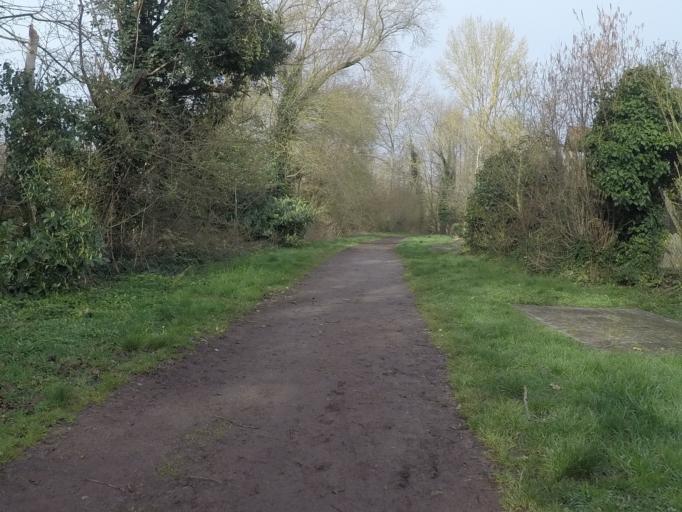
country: DE
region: Rheinland-Pfalz
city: Billigheim-Ingenheim
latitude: 49.1353
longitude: 8.0964
